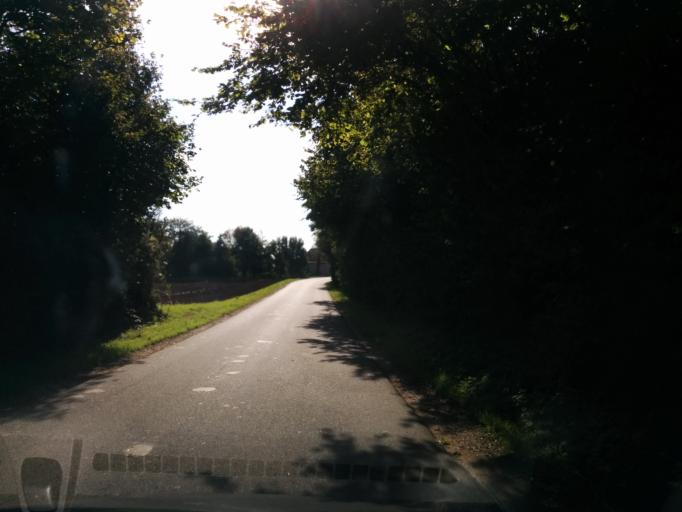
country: DK
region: South Denmark
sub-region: Kolding Kommune
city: Sonder Bjert
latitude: 55.4060
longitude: 9.5514
